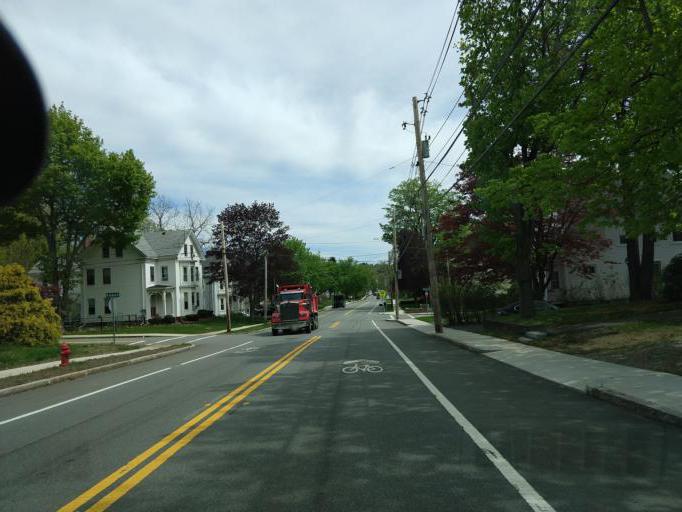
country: US
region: Massachusetts
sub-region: Essex County
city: Merrimac
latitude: 42.8294
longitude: -71.0077
